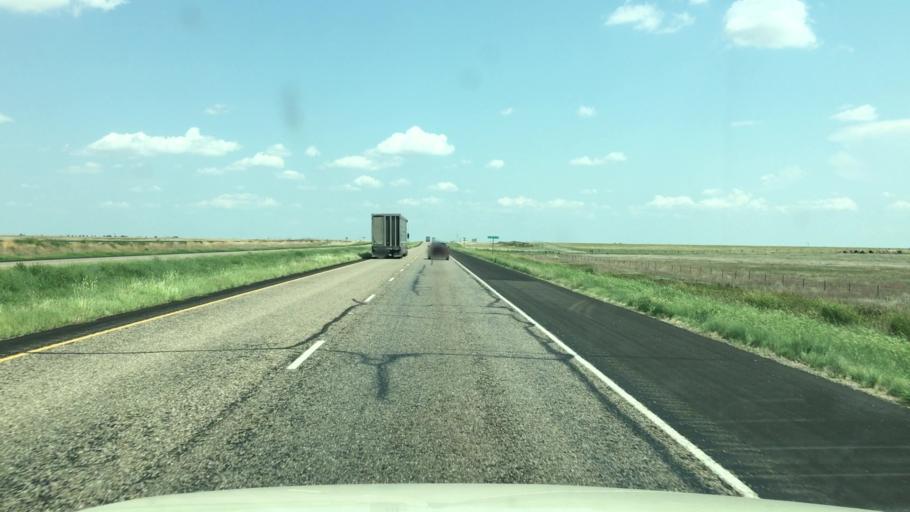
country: US
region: Texas
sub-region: Armstrong County
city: Claude
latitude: 35.1321
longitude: -101.4197
